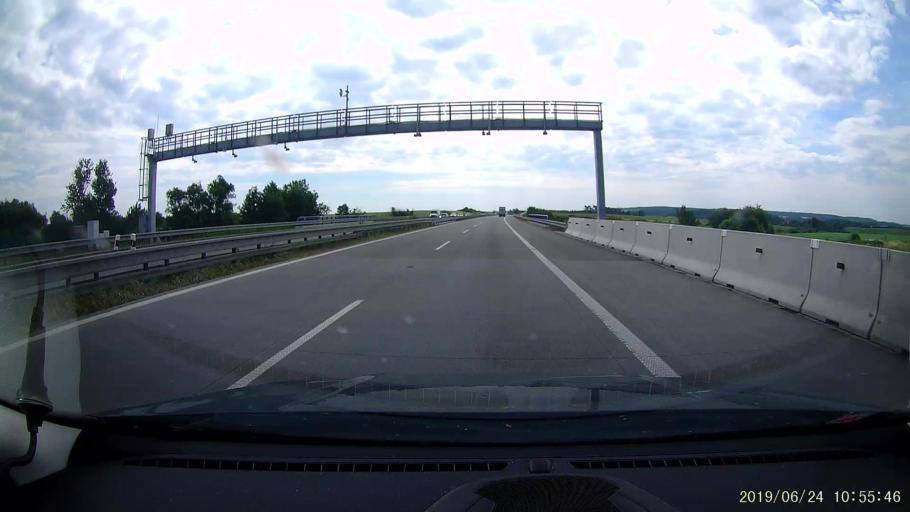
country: CZ
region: Vysocina
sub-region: Okres Zd'ar nad Sazavou
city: Velka Bites
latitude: 49.2993
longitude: 16.1614
